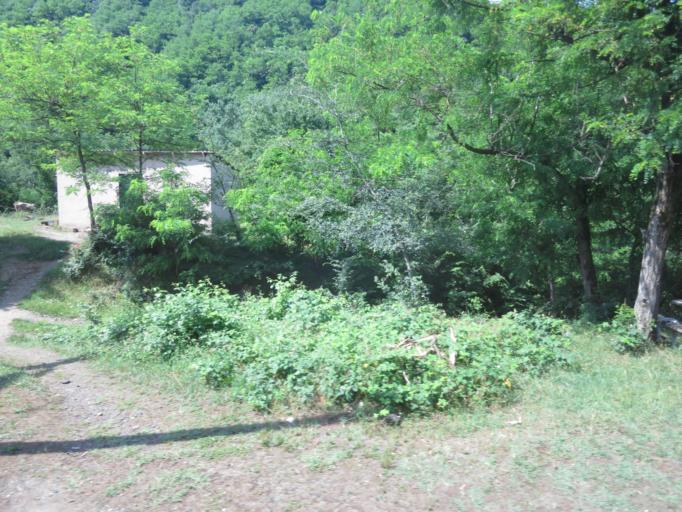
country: GE
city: Shorapani
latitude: 42.0934
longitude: 43.1304
